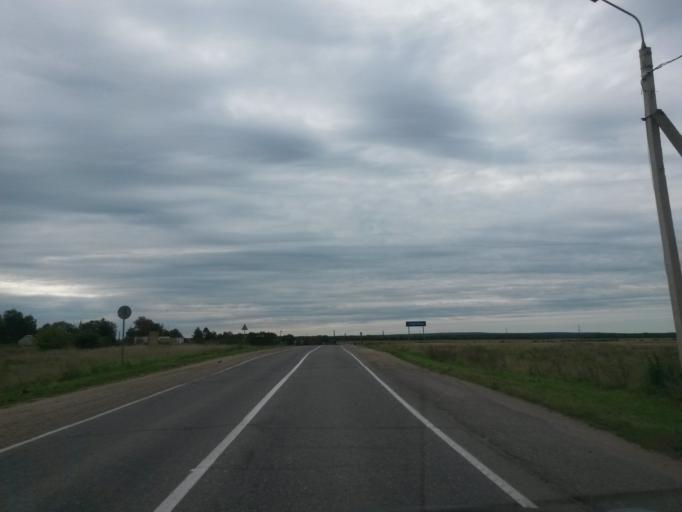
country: RU
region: Jaroslavl
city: Gavrilov-Yam
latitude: 57.3352
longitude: 39.8097
